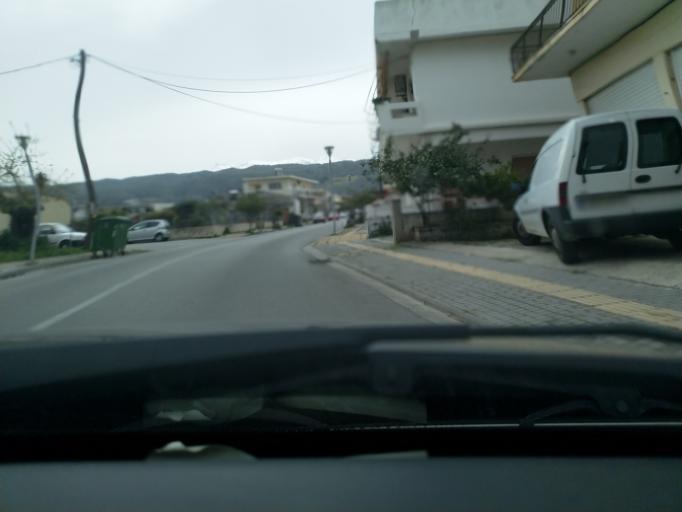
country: GR
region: Crete
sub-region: Nomos Chanias
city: Mournies
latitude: 35.4948
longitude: 24.0227
